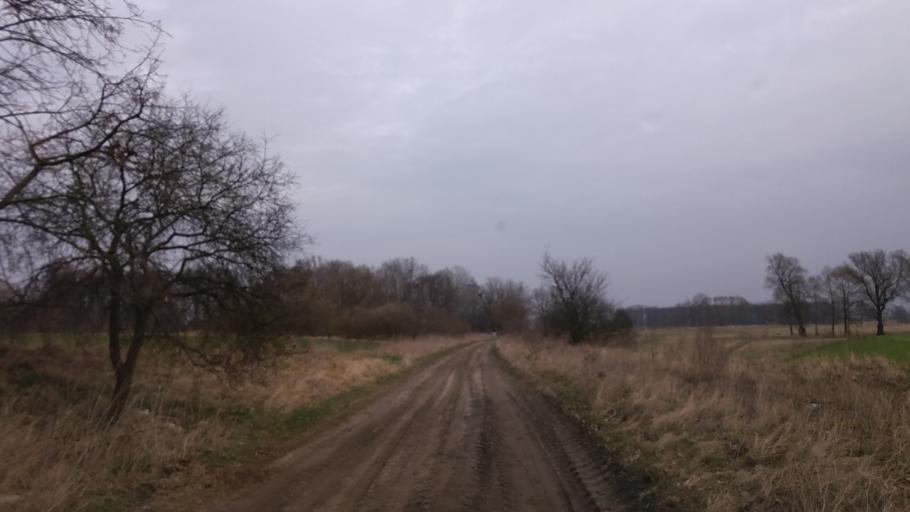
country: PL
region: West Pomeranian Voivodeship
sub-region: Powiat choszczenski
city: Pelczyce
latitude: 53.1110
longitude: 15.3368
